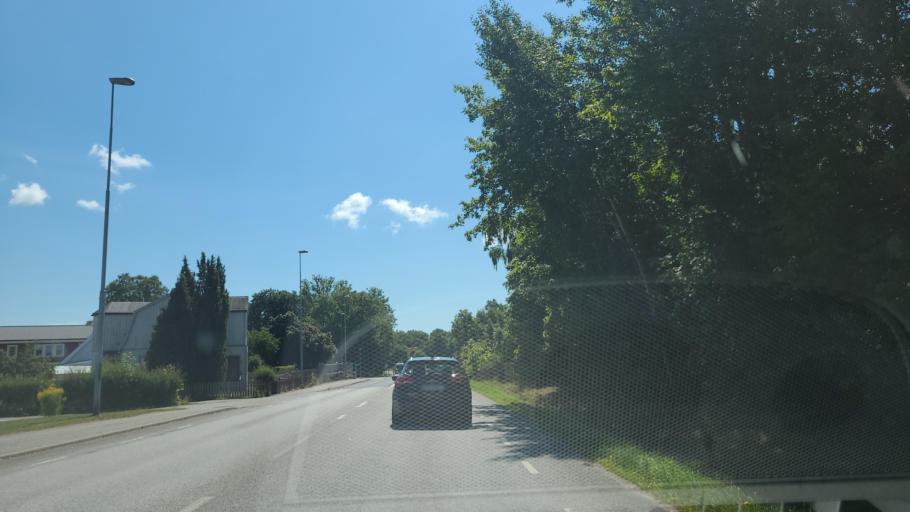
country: SE
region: Blekinge
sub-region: Karlskrona Kommun
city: Rodeby
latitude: 56.2497
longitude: 15.6193
